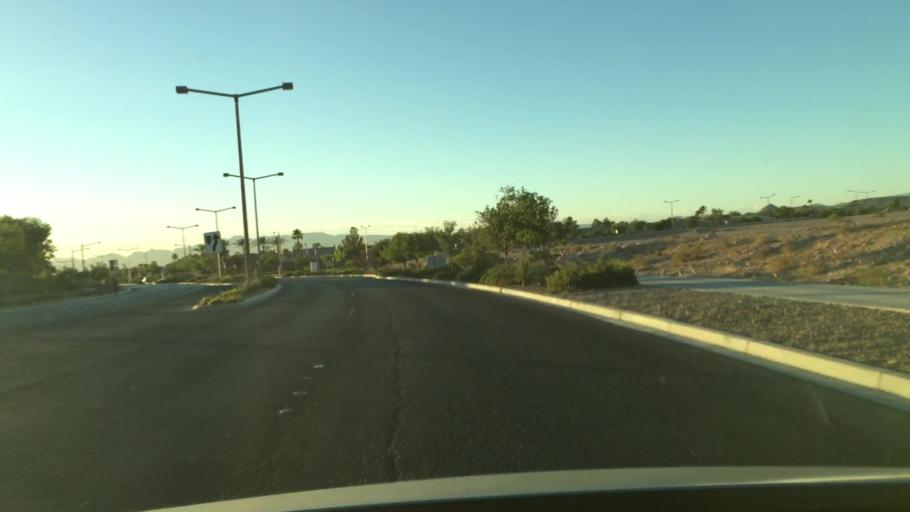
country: US
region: Nevada
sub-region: Clark County
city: Summerlin South
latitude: 36.1011
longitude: -115.3265
